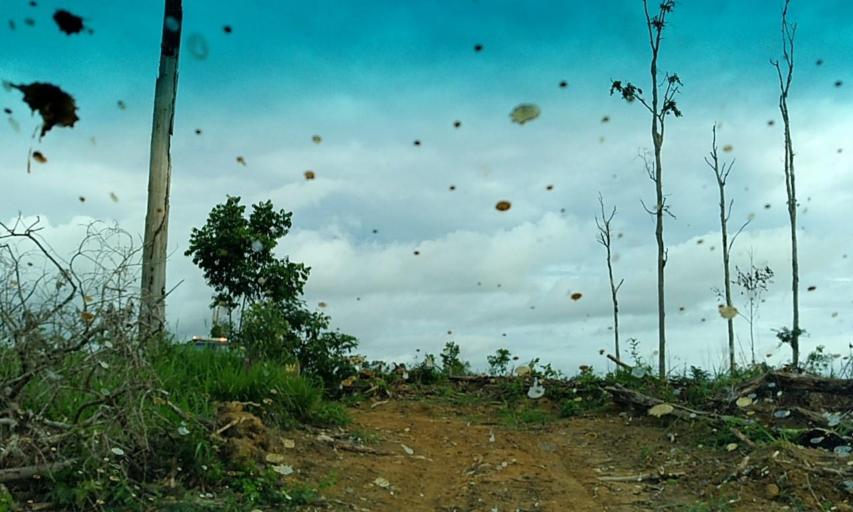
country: BR
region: Para
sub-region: Senador Jose Porfirio
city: Senador Jose Porfirio
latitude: -3.0067
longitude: -51.7522
